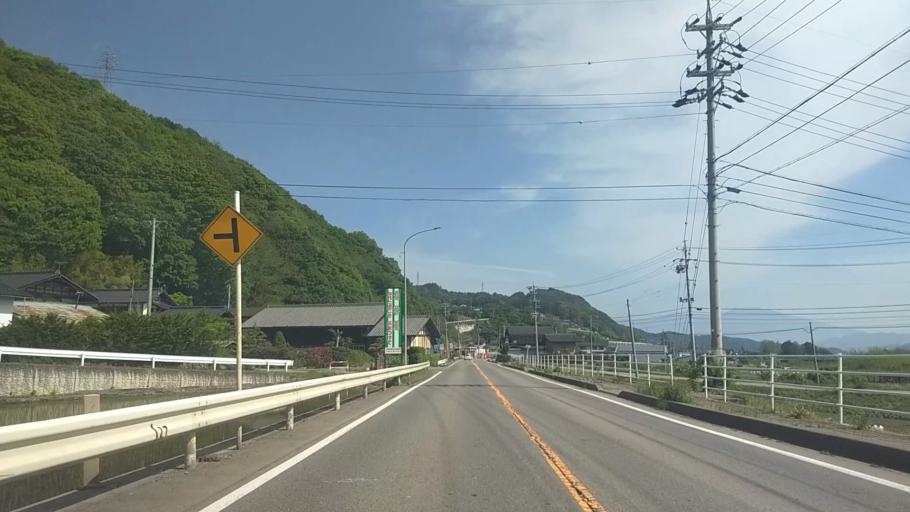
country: JP
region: Nagano
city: Saku
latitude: 36.1226
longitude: 138.4696
